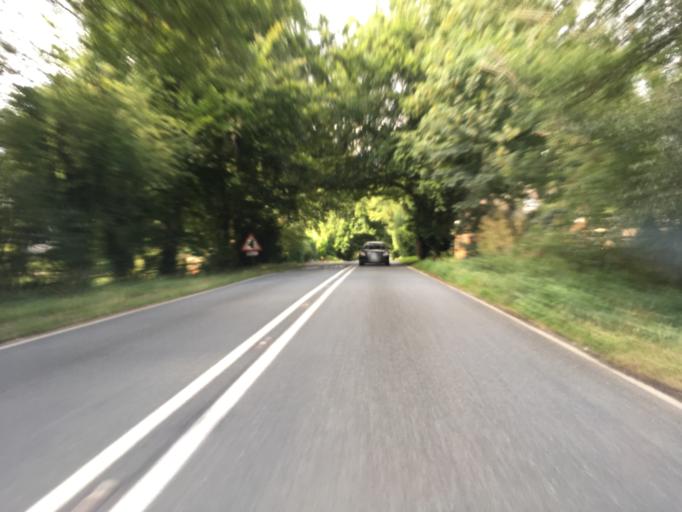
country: GB
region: England
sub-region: Hampshire
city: Kings Worthy
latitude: 51.1478
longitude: -1.2455
